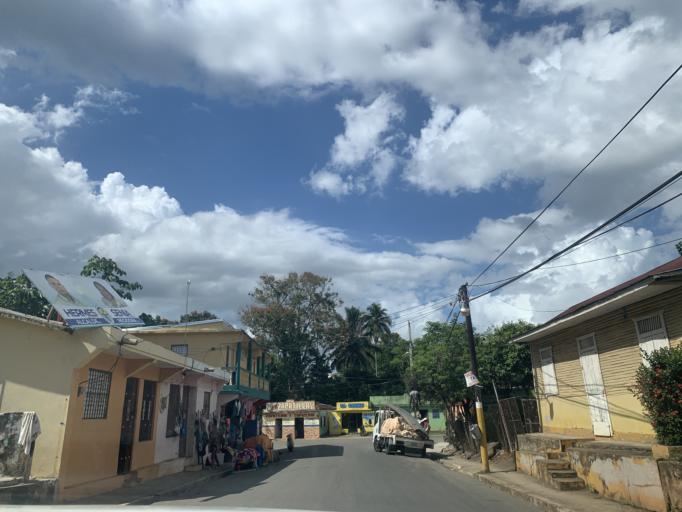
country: DO
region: Monte Plata
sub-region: Yamasa
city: Yamasa
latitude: 18.7715
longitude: -70.0270
